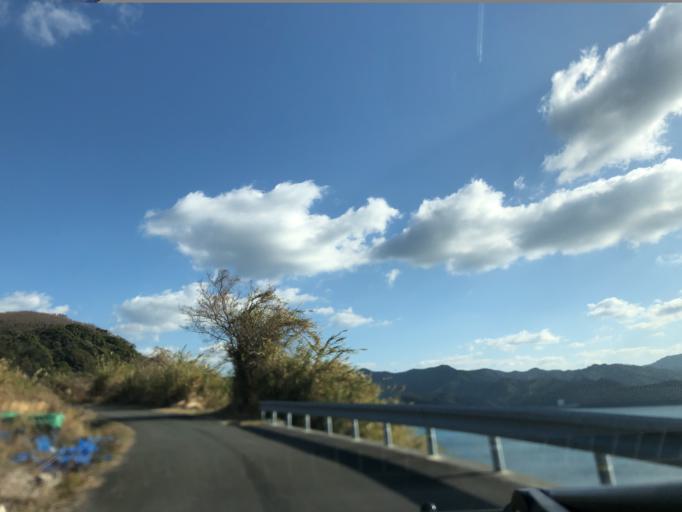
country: JP
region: Kochi
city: Sukumo
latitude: 32.9103
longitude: 132.6959
